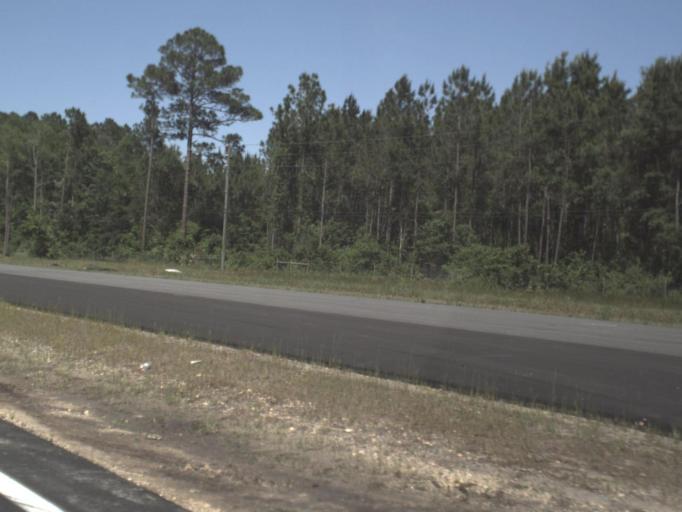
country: US
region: Florida
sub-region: Duval County
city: Baldwin
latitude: 30.3518
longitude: -81.9512
